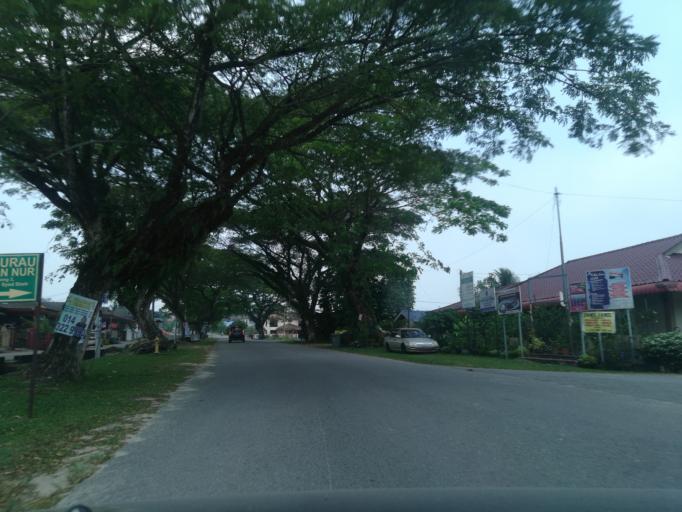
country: MY
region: Kedah
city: Kulim
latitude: 5.4006
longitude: 100.5637
